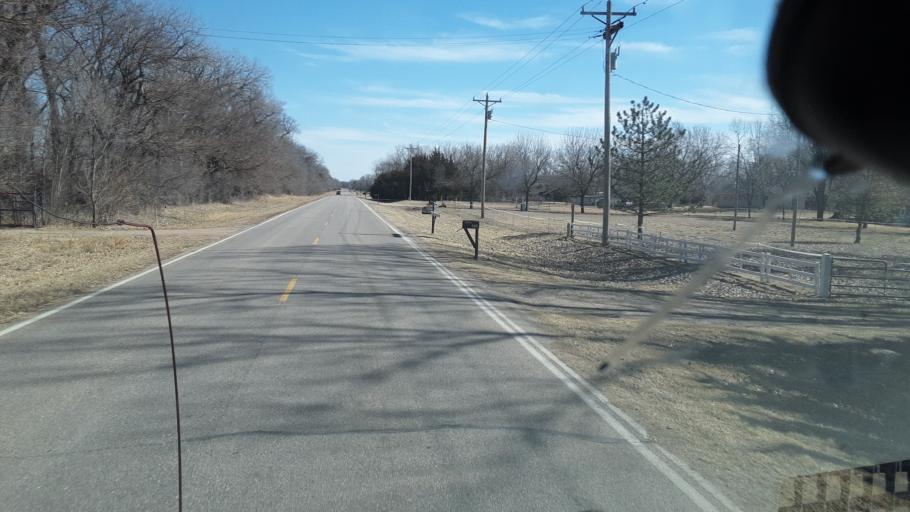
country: US
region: Kansas
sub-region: Reno County
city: Buhler
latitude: 38.1592
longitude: -97.8722
